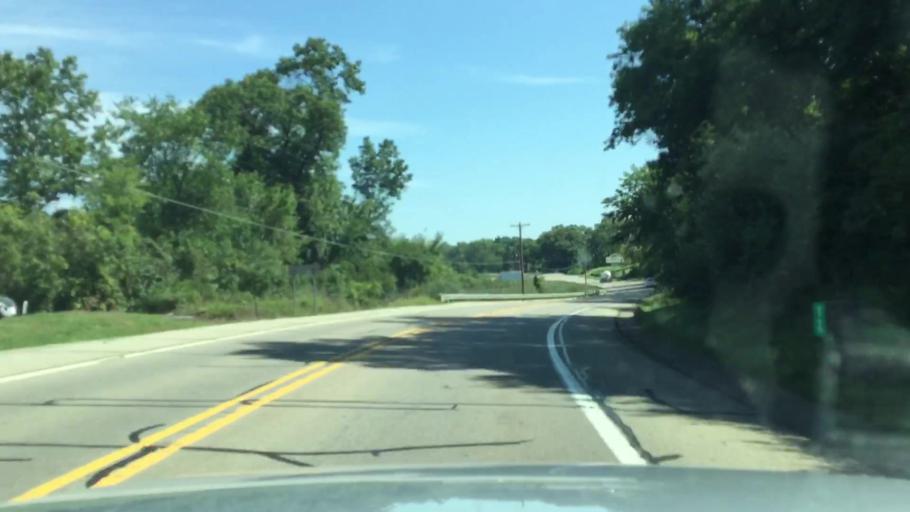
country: US
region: Michigan
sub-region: Washtenaw County
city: Manchester
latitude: 42.0669
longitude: -84.1030
